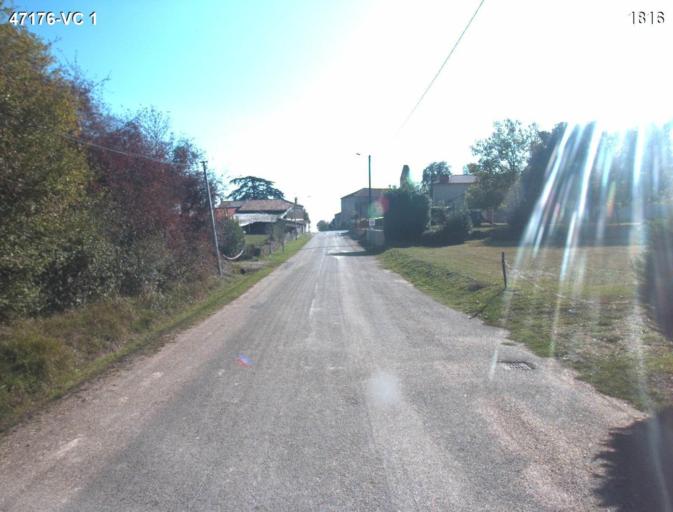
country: FR
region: Aquitaine
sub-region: Departement du Lot-et-Garonne
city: Vianne
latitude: 44.2088
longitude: 0.2947
